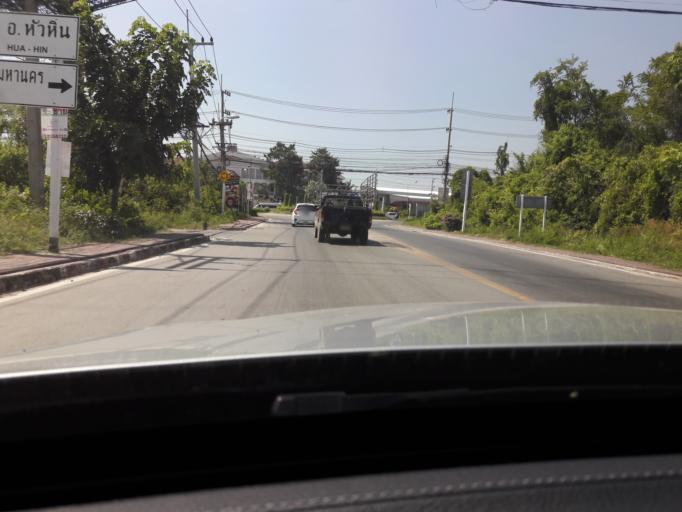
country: TH
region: Phetchaburi
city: Cha-am
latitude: 12.8027
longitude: 99.9738
